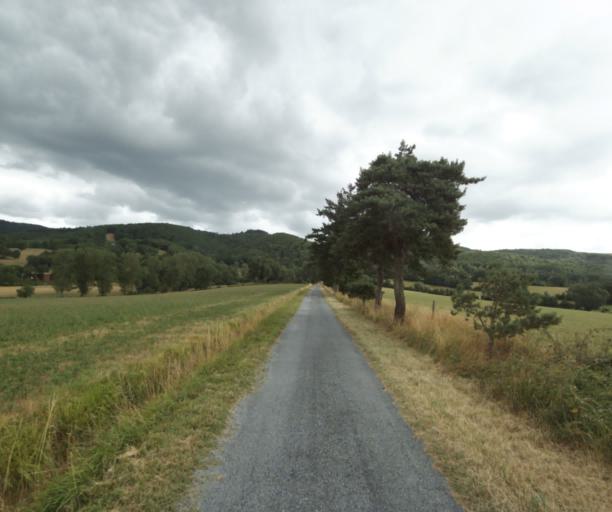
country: FR
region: Midi-Pyrenees
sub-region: Departement du Tarn
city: Soreze
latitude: 43.4624
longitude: 2.0875
